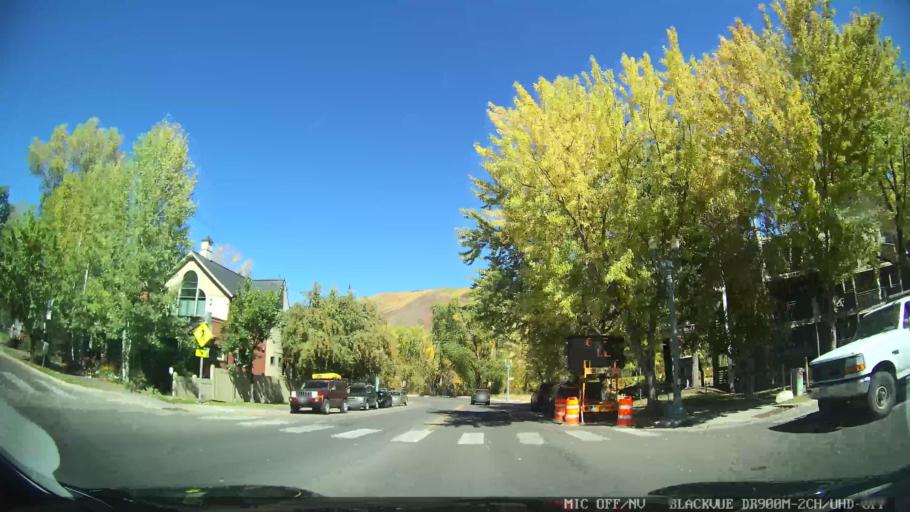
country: US
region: Colorado
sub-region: Pitkin County
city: Aspen
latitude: 39.1887
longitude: -106.8148
